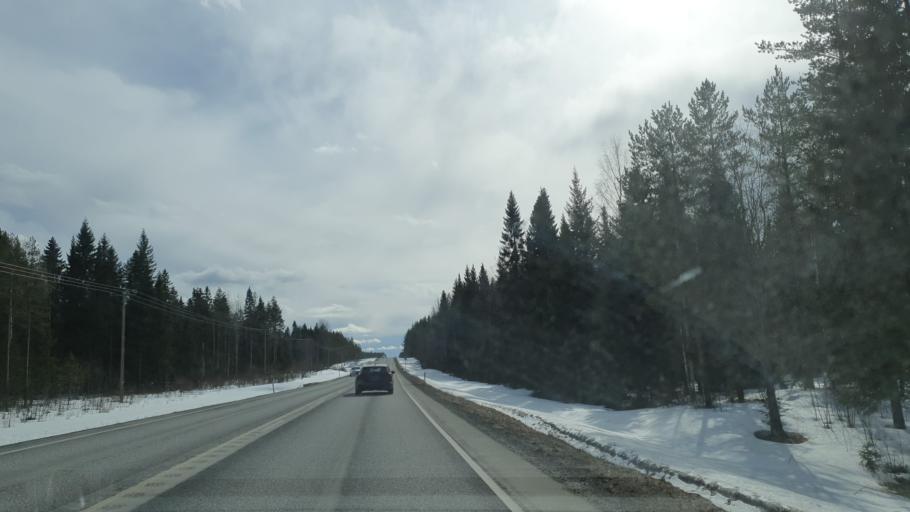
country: FI
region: Kainuu
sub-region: Kajaani
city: Ristijaervi
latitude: 64.3617
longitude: 28.0487
